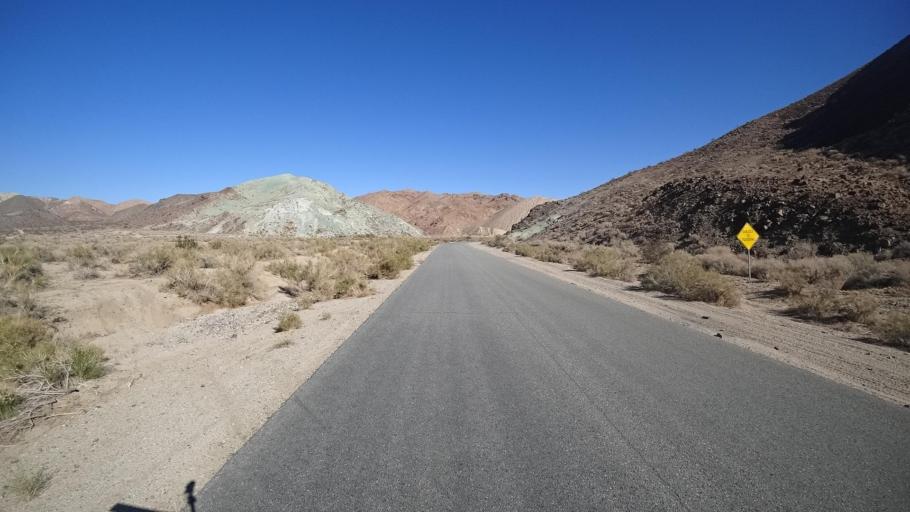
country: US
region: California
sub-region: Kern County
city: California City
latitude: 35.3168
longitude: -118.0851
